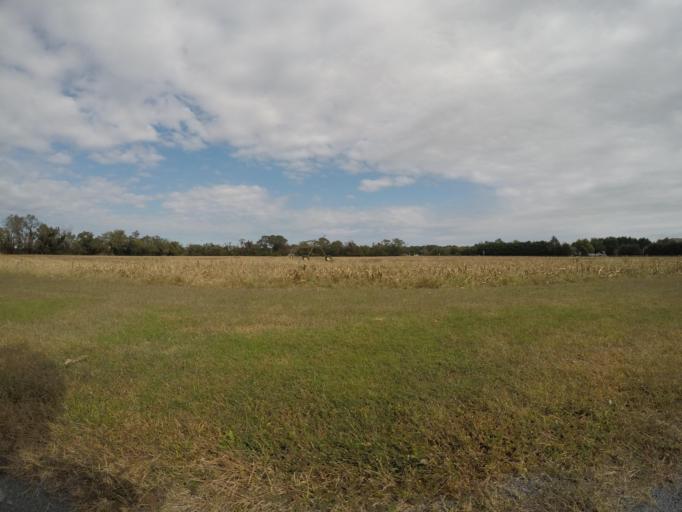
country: US
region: Delaware
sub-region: Sussex County
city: Rehoboth Beach
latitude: 38.7223
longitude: -75.1065
